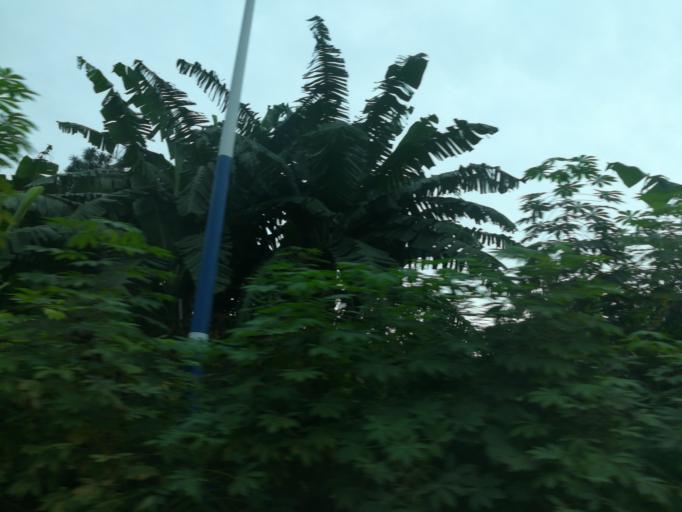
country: NG
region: Rivers
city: Port Harcourt
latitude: 4.8194
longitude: 7.0258
